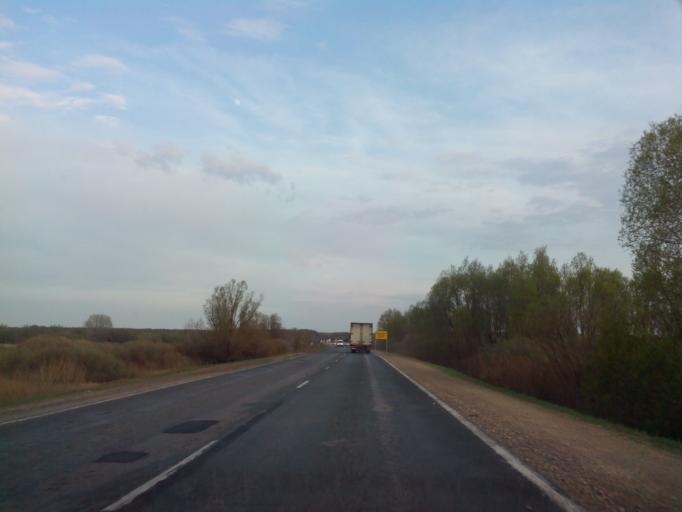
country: RU
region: Rjazan
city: Ryazhsk
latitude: 53.7191
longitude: 39.9159
